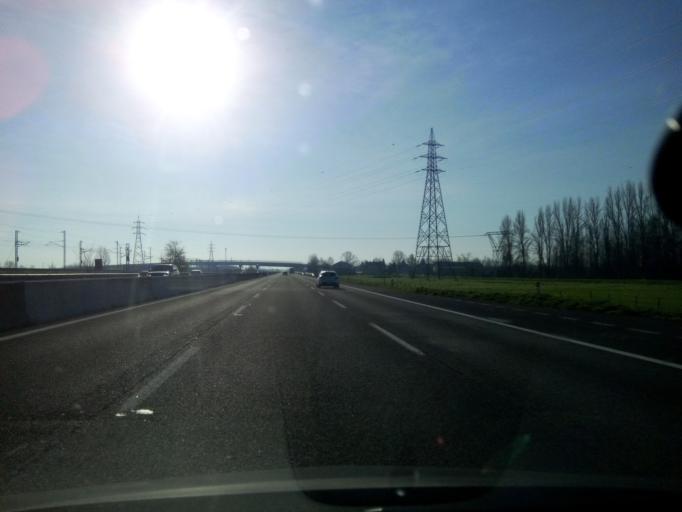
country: IT
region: Emilia-Romagna
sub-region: Provincia di Reggio Emilia
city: Prato
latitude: 44.6926
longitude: 10.7721
